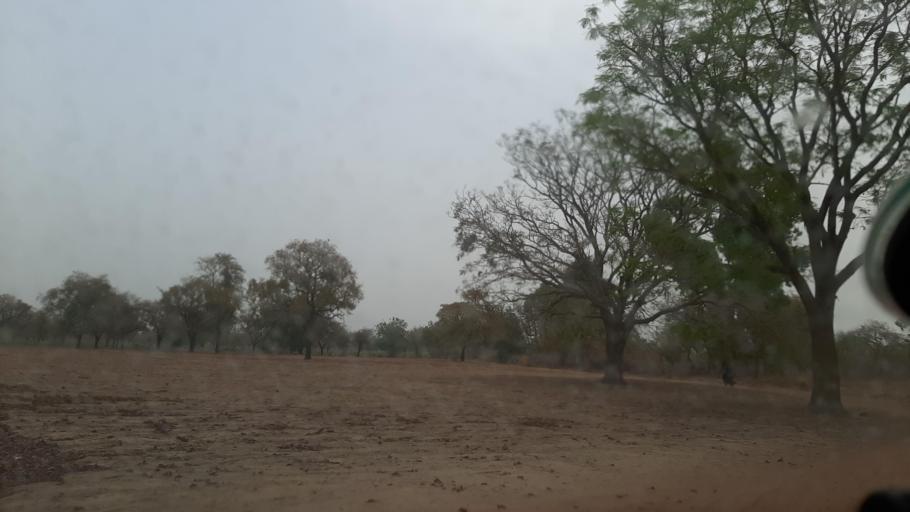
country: BF
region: Boucle du Mouhoun
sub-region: Province des Banwa
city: Salanso
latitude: 11.8501
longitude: -4.4245
